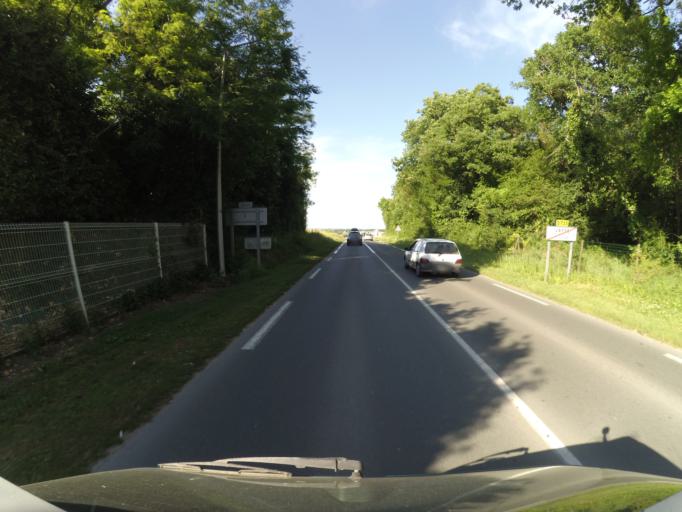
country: FR
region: Poitou-Charentes
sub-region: Departement de la Charente-Maritime
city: Saint-Sulpice-de-Royan
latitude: 45.6602
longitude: -1.0190
